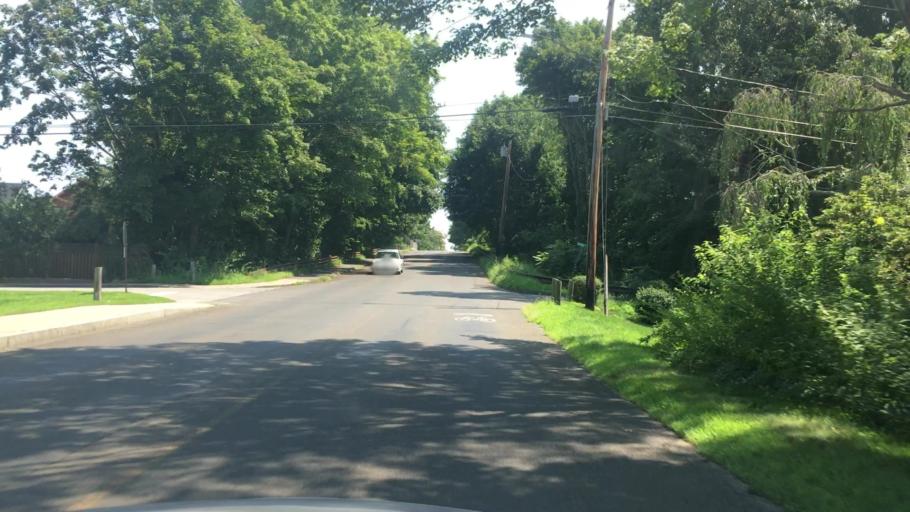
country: US
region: Connecticut
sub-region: New Haven County
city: Guilford Center
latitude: 41.2768
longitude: -72.6763
